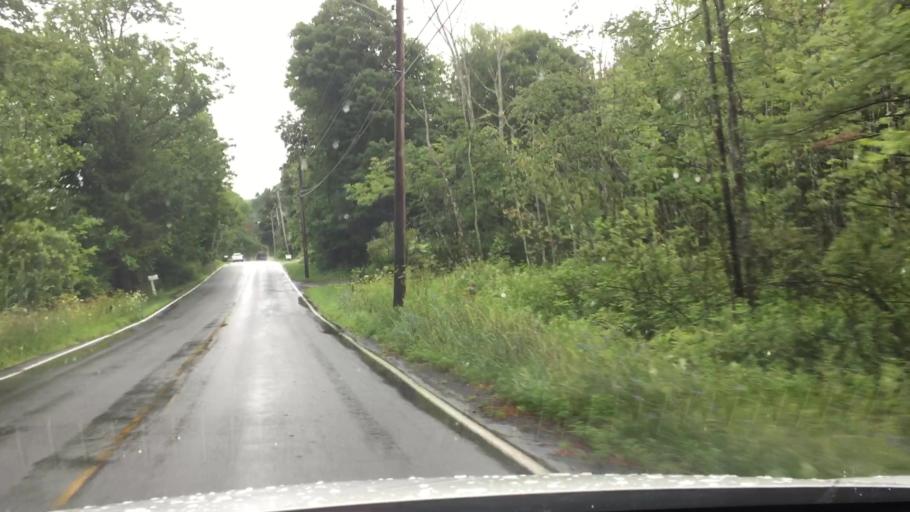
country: US
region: Massachusetts
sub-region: Berkshire County
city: Pittsfield
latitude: 42.4200
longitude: -73.2883
